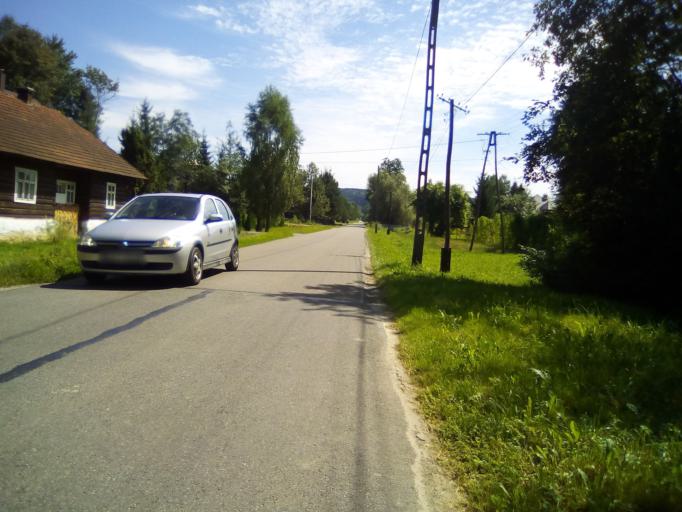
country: PL
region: Subcarpathian Voivodeship
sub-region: Powiat strzyzowski
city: Konieczkowa
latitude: 49.8390
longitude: 21.9287
